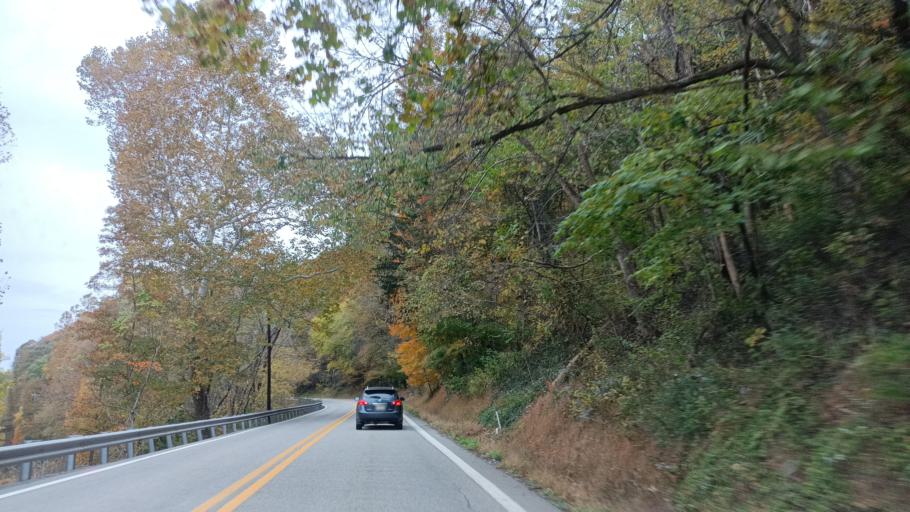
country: US
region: West Virginia
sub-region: Taylor County
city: Grafton
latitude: 39.3448
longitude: -79.9533
